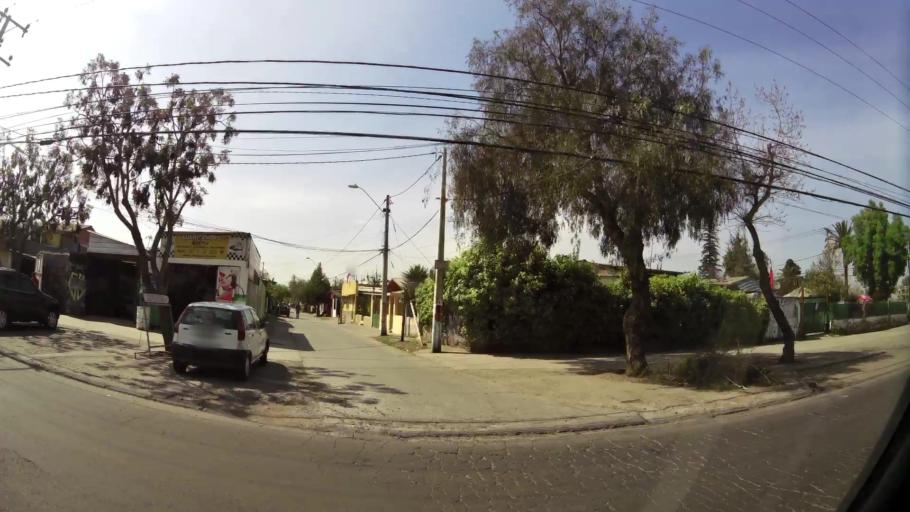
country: CL
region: Santiago Metropolitan
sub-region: Provincia de Santiago
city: Lo Prado
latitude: -33.4362
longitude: -70.7519
